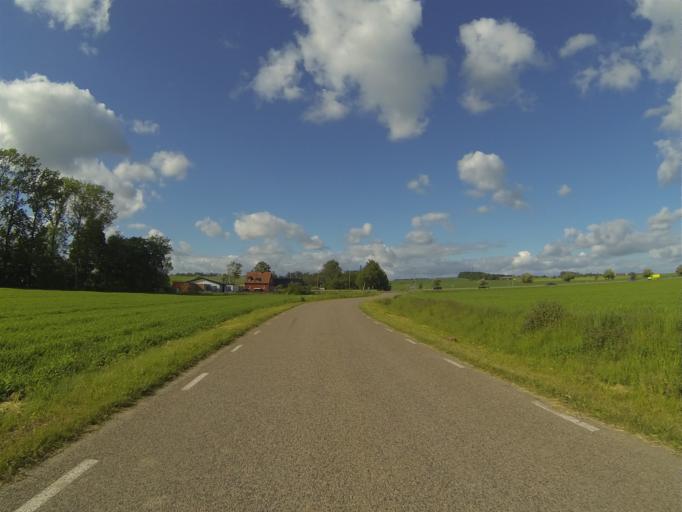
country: SE
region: Skane
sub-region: Staffanstorps Kommun
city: Staffanstorp
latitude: 55.6833
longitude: 13.2674
